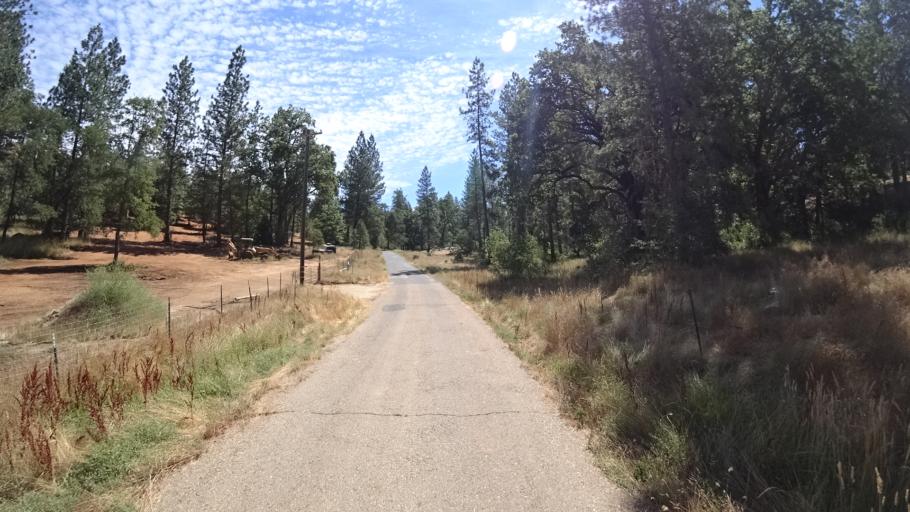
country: US
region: California
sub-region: Calaveras County
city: Mountain Ranch
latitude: 38.3373
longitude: -120.4967
